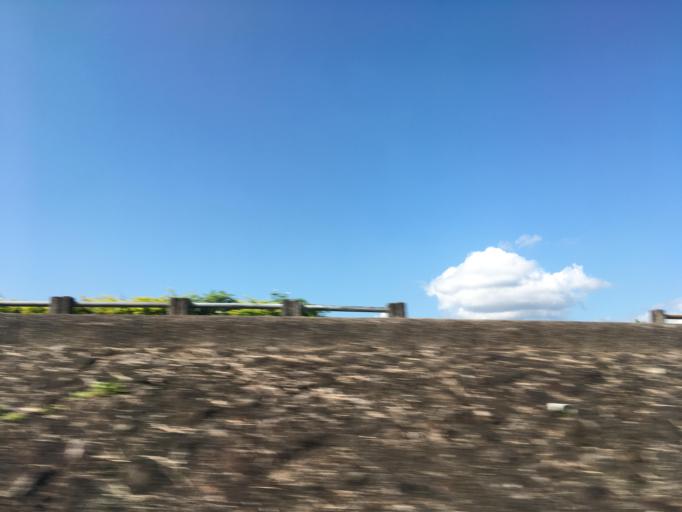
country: TW
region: Taiwan
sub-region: Yilan
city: Yilan
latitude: 24.7538
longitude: 121.7326
